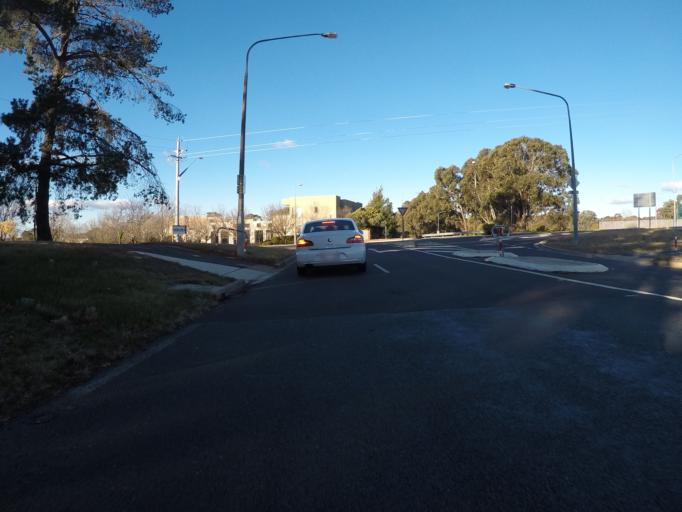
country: AU
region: Australian Capital Territory
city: Forrest
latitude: -35.3133
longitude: 149.0978
